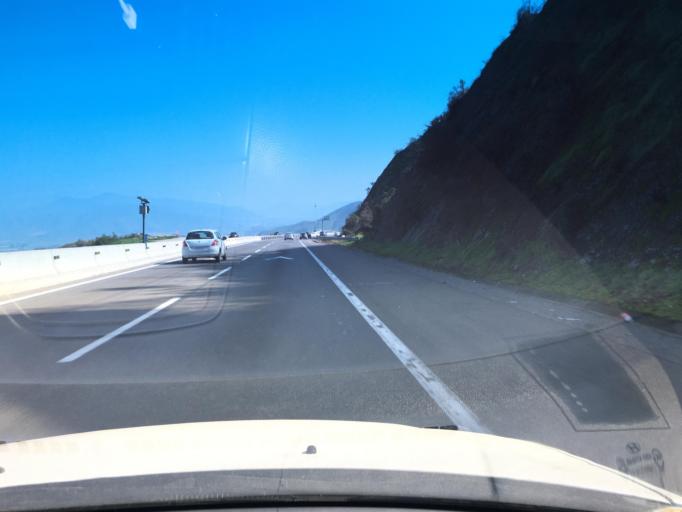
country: CL
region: Santiago Metropolitan
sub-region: Provincia de Talagante
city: Penaflor
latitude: -33.4528
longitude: -70.9747
